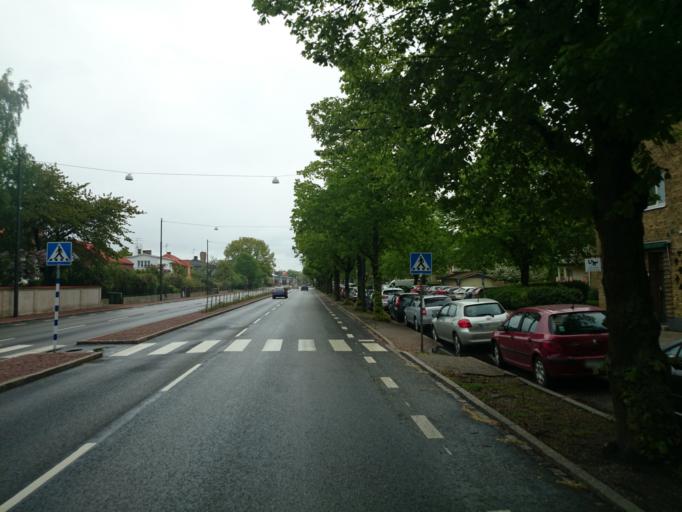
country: SE
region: Skane
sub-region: Malmo
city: Malmoe
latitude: 55.5914
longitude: 12.9626
